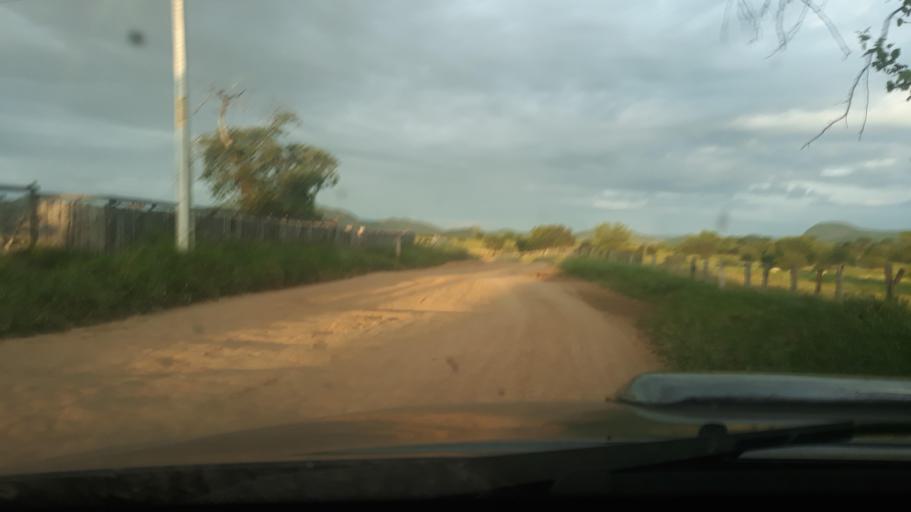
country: BR
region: Bahia
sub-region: Riacho De Santana
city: Riacho de Santana
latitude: -13.8999
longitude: -42.8793
